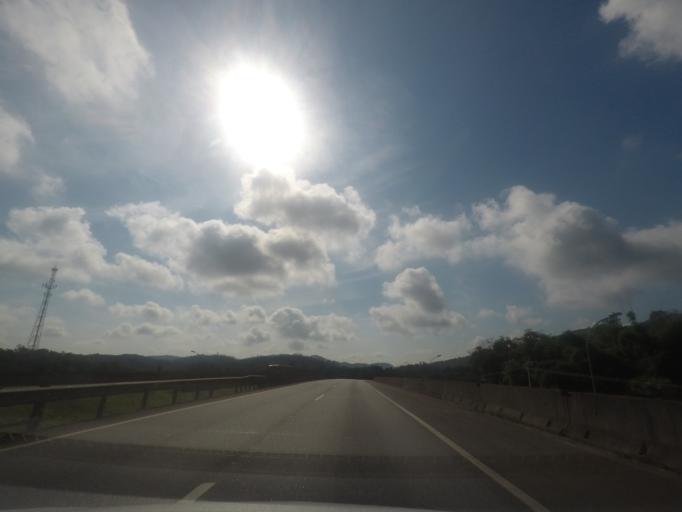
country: BR
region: Parana
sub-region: Antonina
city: Antonina
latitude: -25.5478
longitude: -48.7914
